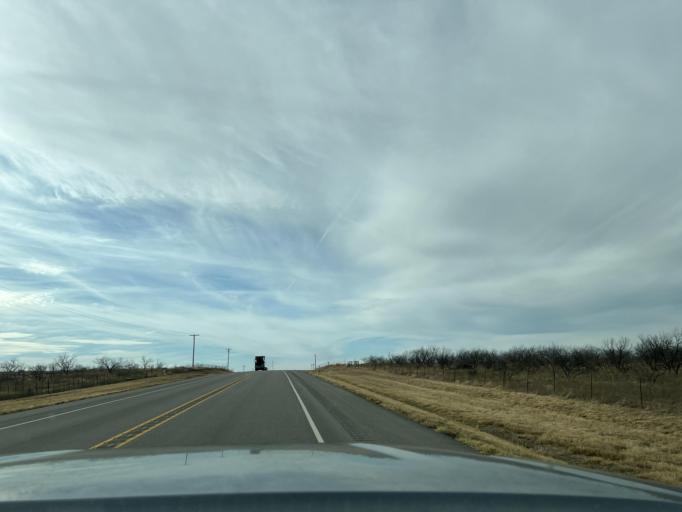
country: US
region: Texas
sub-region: Jones County
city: Anson
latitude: 32.7506
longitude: -99.6976
